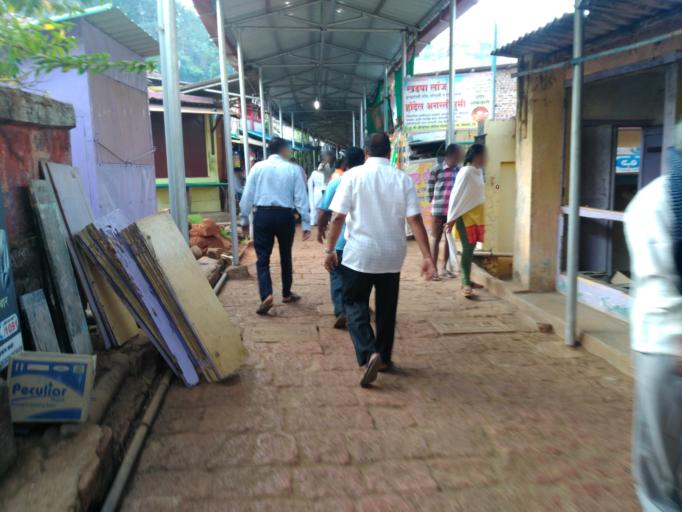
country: IN
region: Maharashtra
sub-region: Raigarh
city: Srivardhan
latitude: 17.9937
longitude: 73.0225
